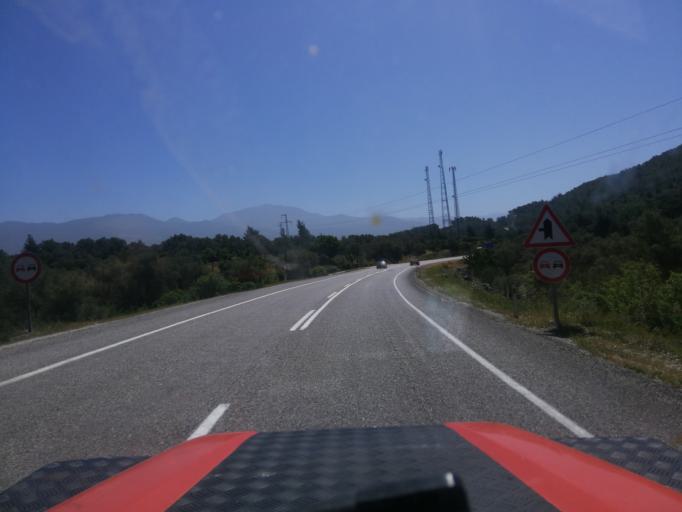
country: TR
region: Mugla
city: Esen
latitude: 36.4092
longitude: 29.2808
